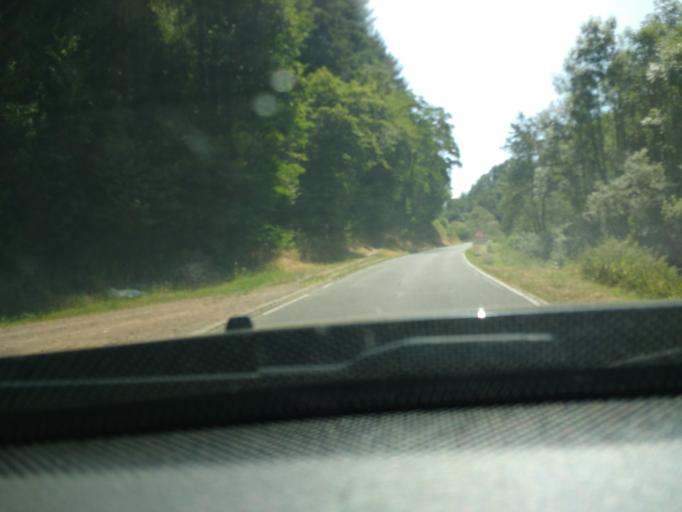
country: DE
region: Rheinland-Pfalz
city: Meerfeld
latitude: 50.0920
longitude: 6.7531
